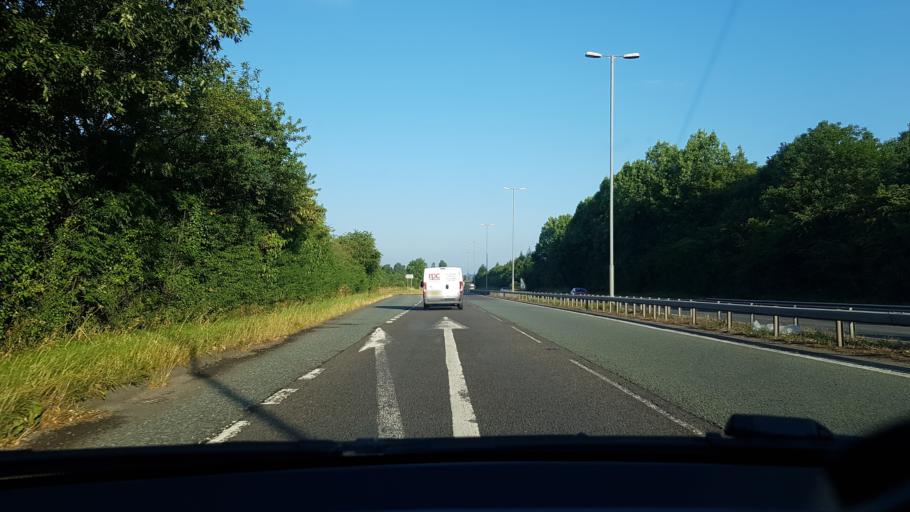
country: GB
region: England
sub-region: Nottinghamshire
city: Eastwood
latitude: 53.0022
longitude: -1.2914
